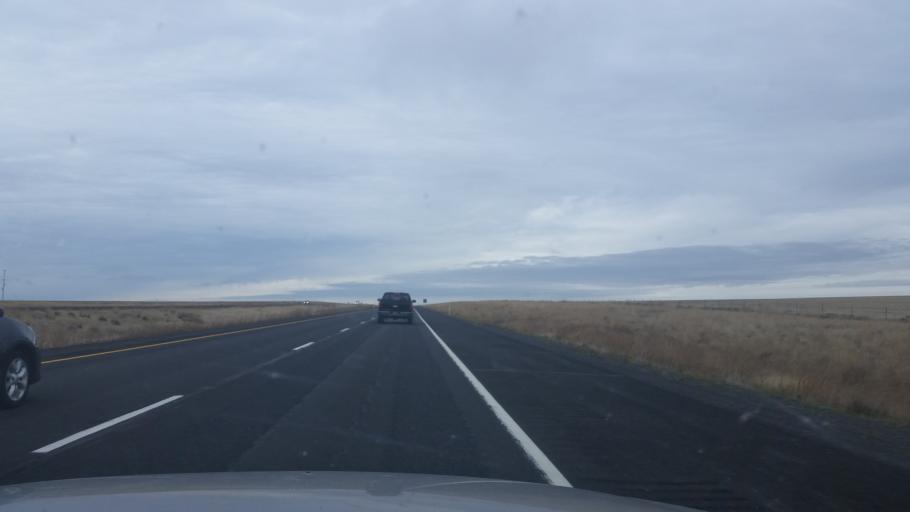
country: US
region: Washington
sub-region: Adams County
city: Ritzville
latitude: 47.1116
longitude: -118.4593
